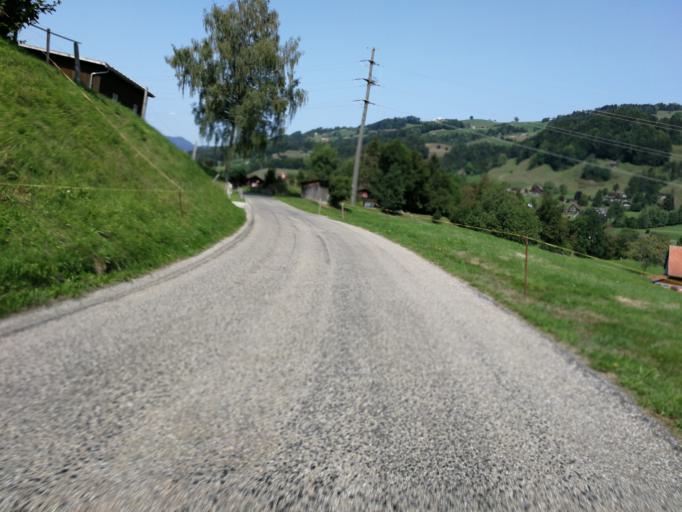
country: CH
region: Saint Gallen
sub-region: Wahlkreis Toggenburg
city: Krummenau
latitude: 47.2516
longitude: 9.1482
